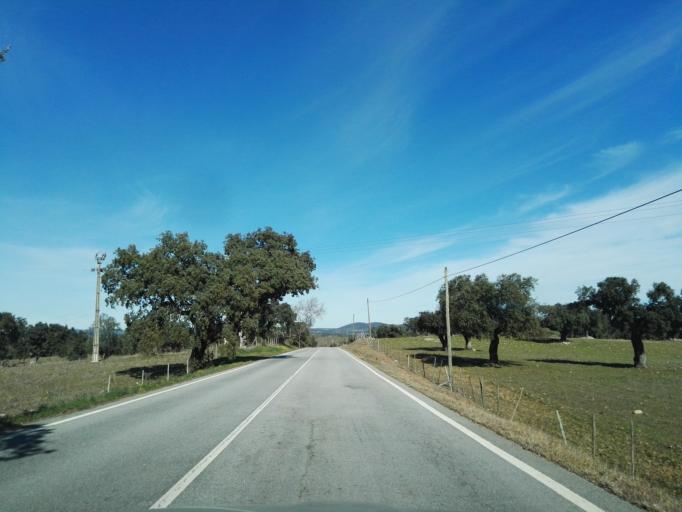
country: PT
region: Portalegre
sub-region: Arronches
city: Arronches
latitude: 39.0997
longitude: -7.2794
